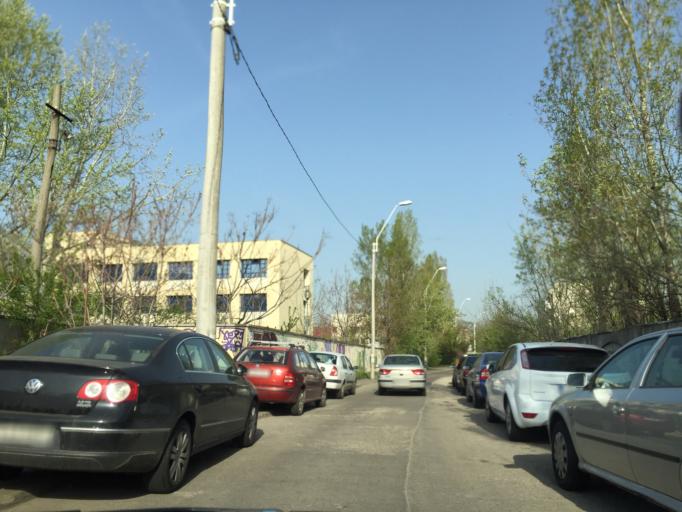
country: RO
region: Bucuresti
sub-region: Municipiul Bucuresti
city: Bucuresti
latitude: 44.4263
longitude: 26.0737
